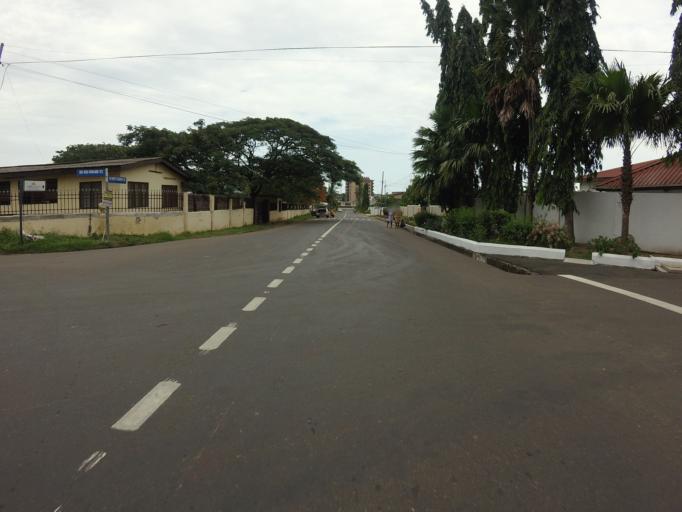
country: GH
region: Greater Accra
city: Dome
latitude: 5.6141
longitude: -0.2045
